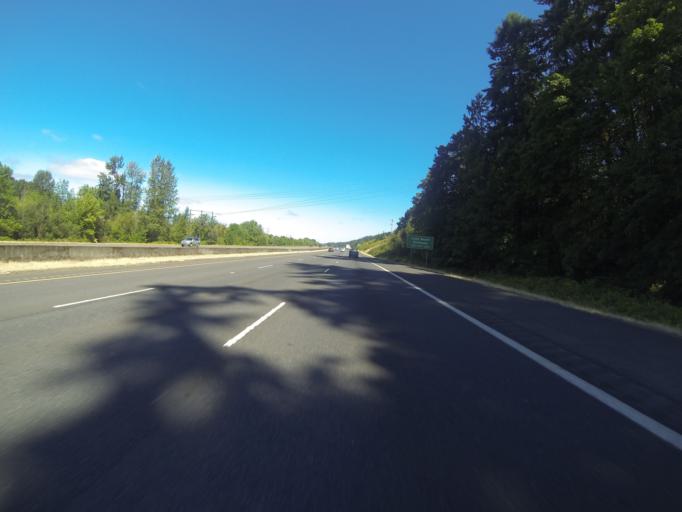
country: US
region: Oregon
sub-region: Columbia County
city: Rainier
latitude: 46.0827
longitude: -122.8670
